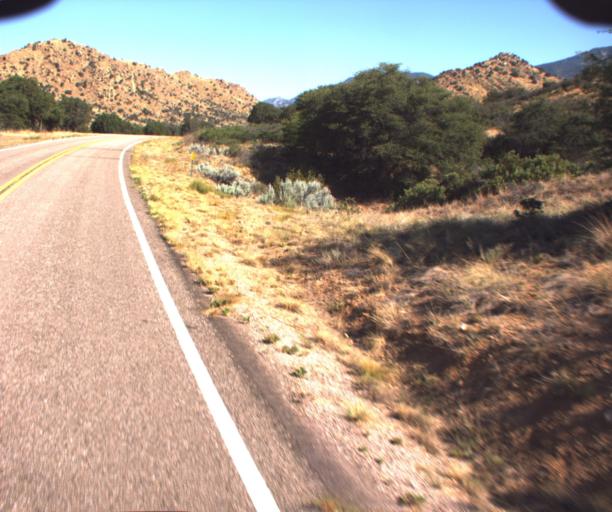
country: US
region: Arizona
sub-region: Graham County
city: Swift Trail Junction
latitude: 32.5783
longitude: -109.8491
